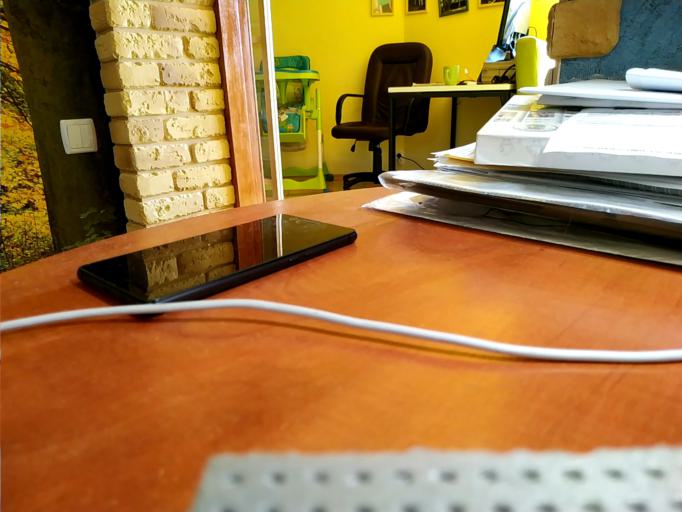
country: RU
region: Tverskaya
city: Kalashnikovo
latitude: 57.3859
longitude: 35.3197
